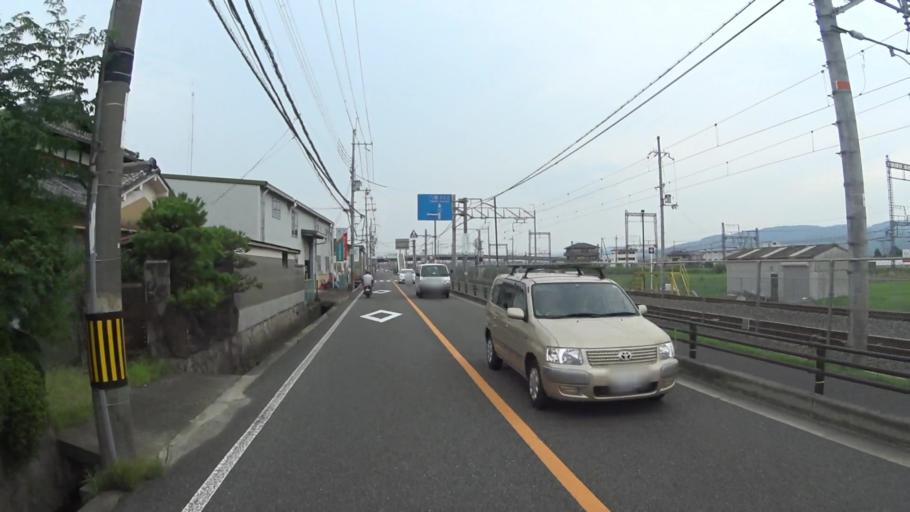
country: JP
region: Kyoto
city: Tanabe
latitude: 34.7648
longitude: 135.7913
